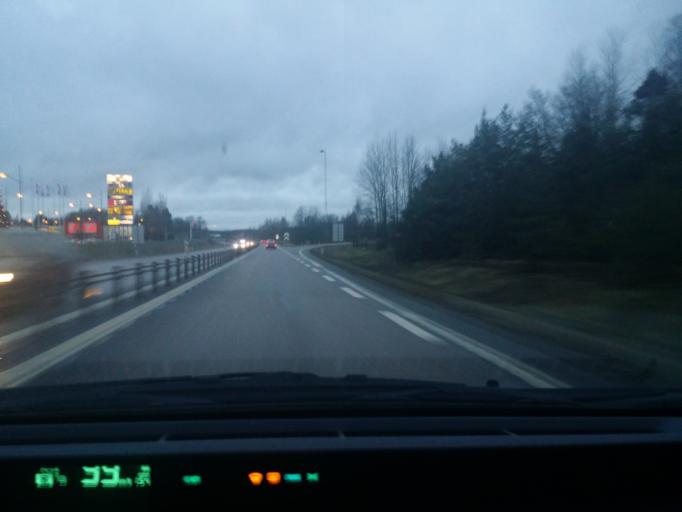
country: SE
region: Soedermanland
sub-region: Eskilstuna Kommun
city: Hallbybrunn
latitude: 59.4025
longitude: 16.4275
